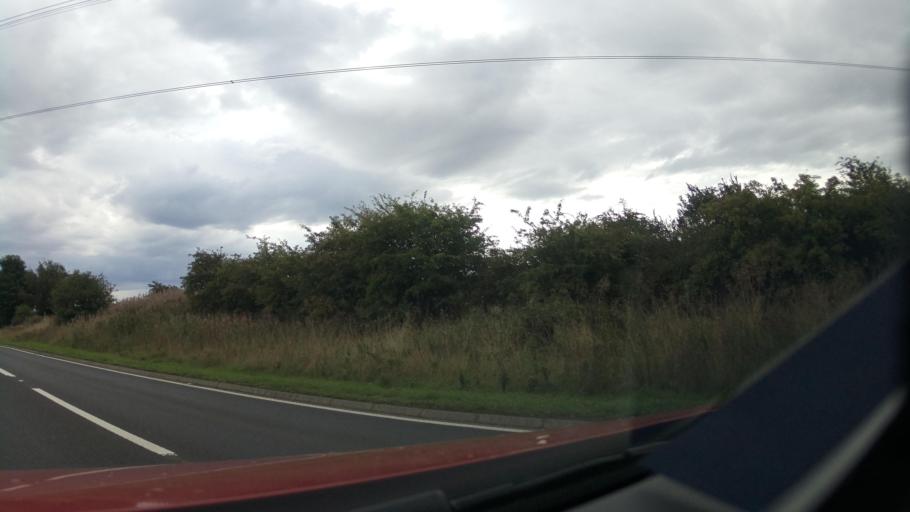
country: GB
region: Scotland
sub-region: Fife
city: High Valleyfield
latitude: 56.0662
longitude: -3.6219
